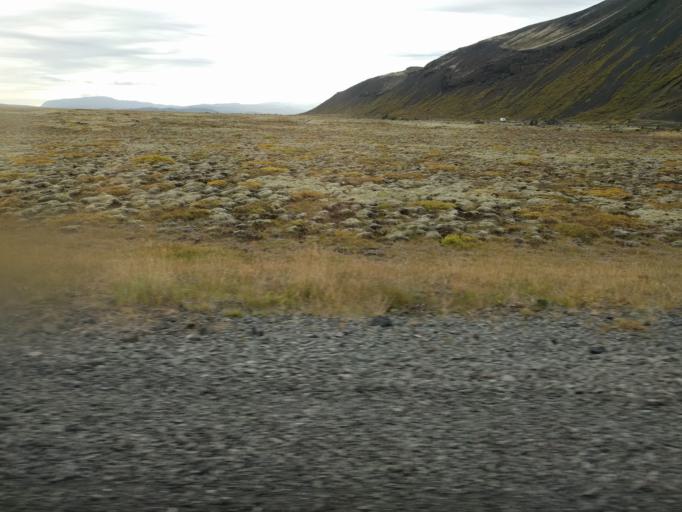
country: IS
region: South
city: Hveragerdi
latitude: 64.1956
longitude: -21.0226
